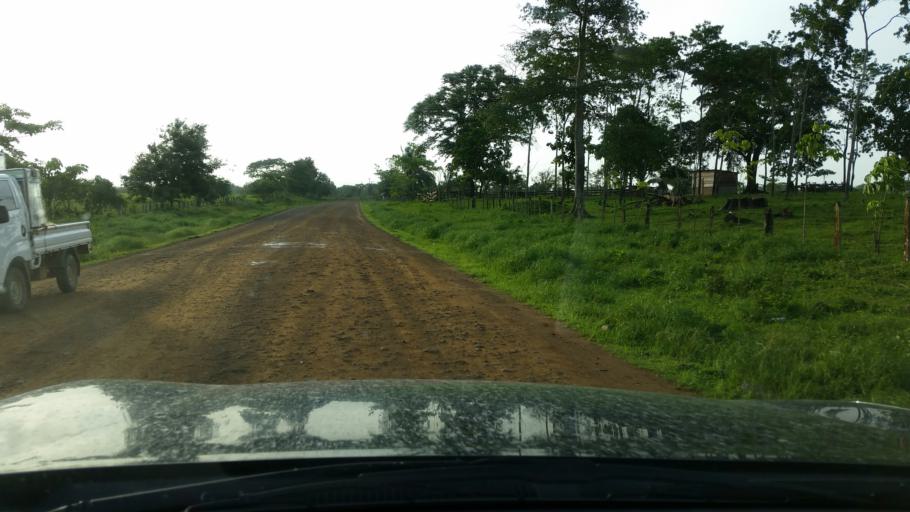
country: NI
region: Atlantico Norte (RAAN)
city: Bonanza
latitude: 14.0654
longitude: -84.0027
